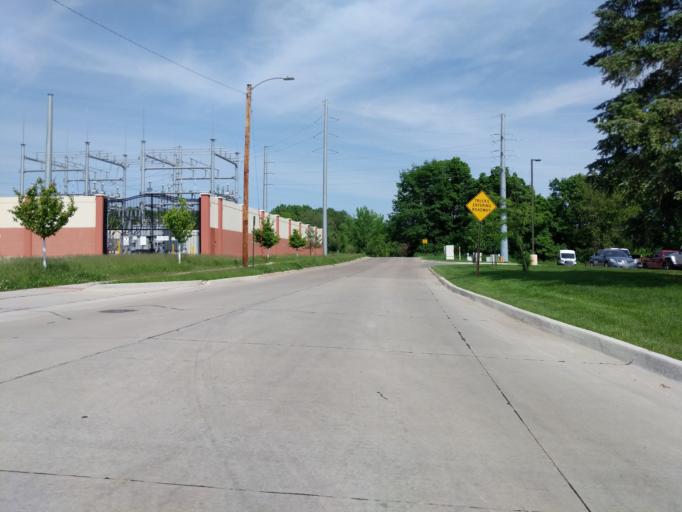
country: US
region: Iowa
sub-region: Linn County
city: Cedar Rapids
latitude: 42.0171
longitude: -91.6335
